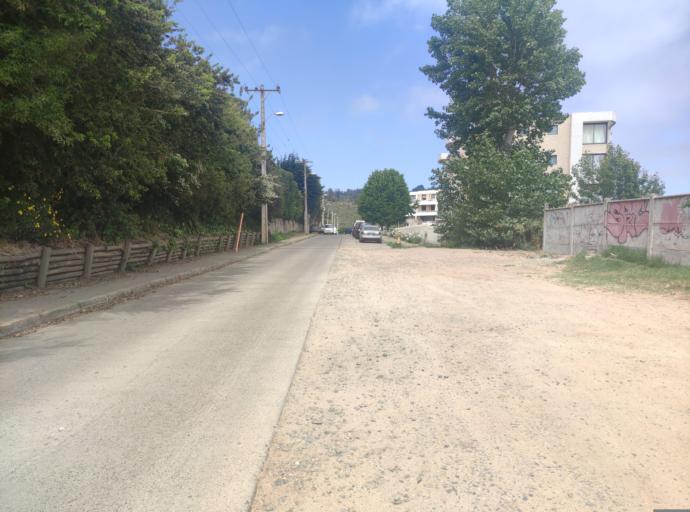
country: CL
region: Valparaiso
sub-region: Provincia de Valparaiso
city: Vina del Mar
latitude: -32.9691
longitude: -71.5256
